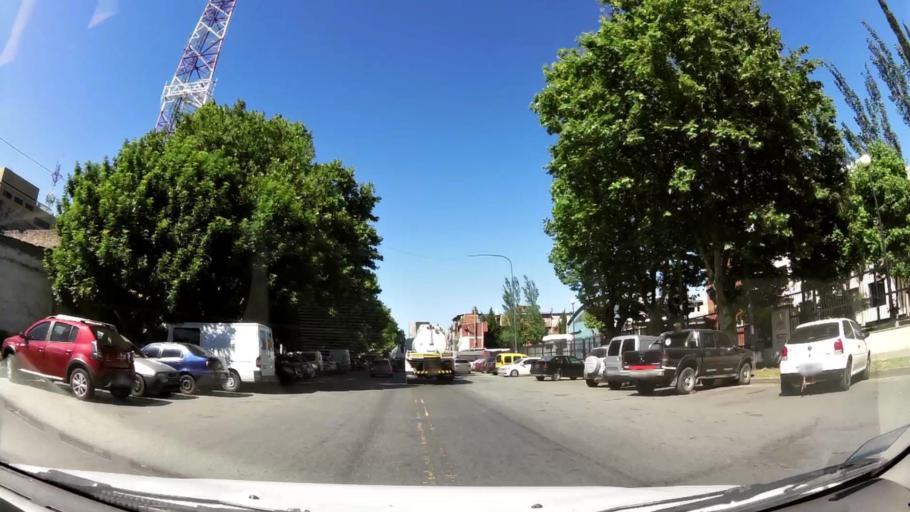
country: AR
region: Buenos Aires F.D.
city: Retiro
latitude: -34.5815
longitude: -58.3758
